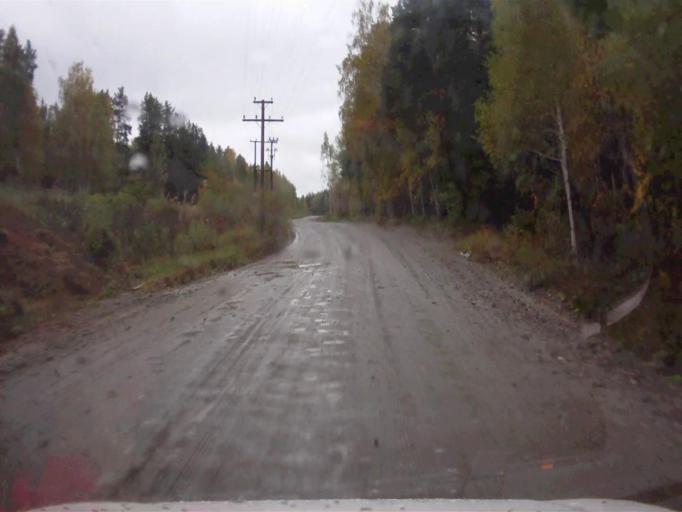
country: RU
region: Chelyabinsk
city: Kyshtym
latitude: 55.8008
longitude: 60.4798
